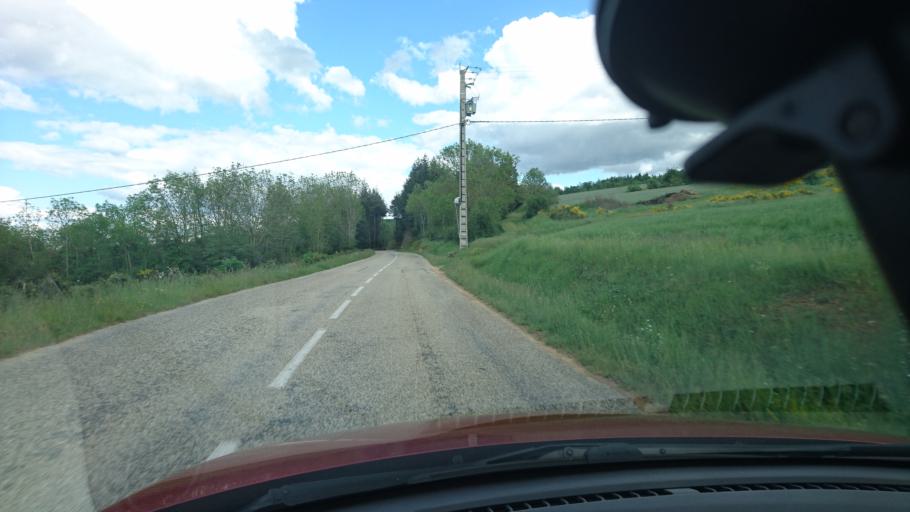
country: FR
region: Rhone-Alpes
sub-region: Departement de la Loire
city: Maclas
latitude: 45.3433
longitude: 4.6923
